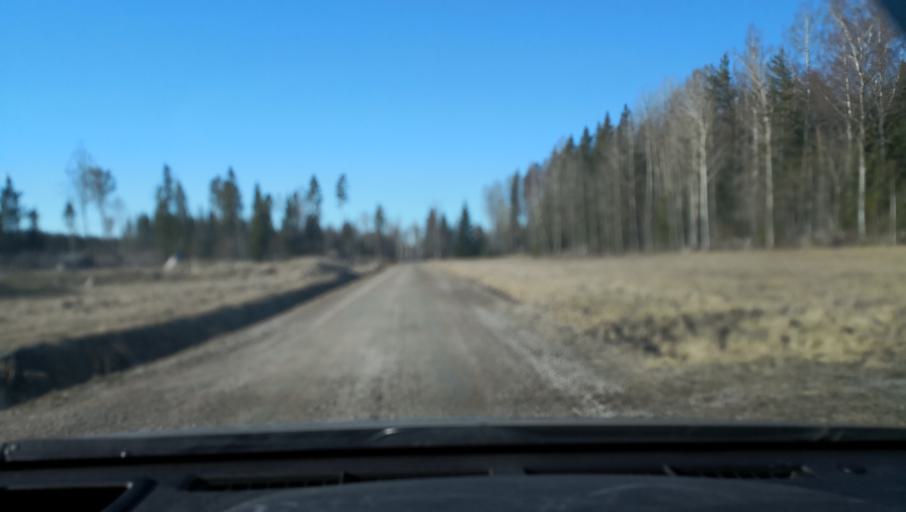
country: SE
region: Dalarna
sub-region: Avesta Kommun
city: Horndal
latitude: 60.1742
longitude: 16.6322
